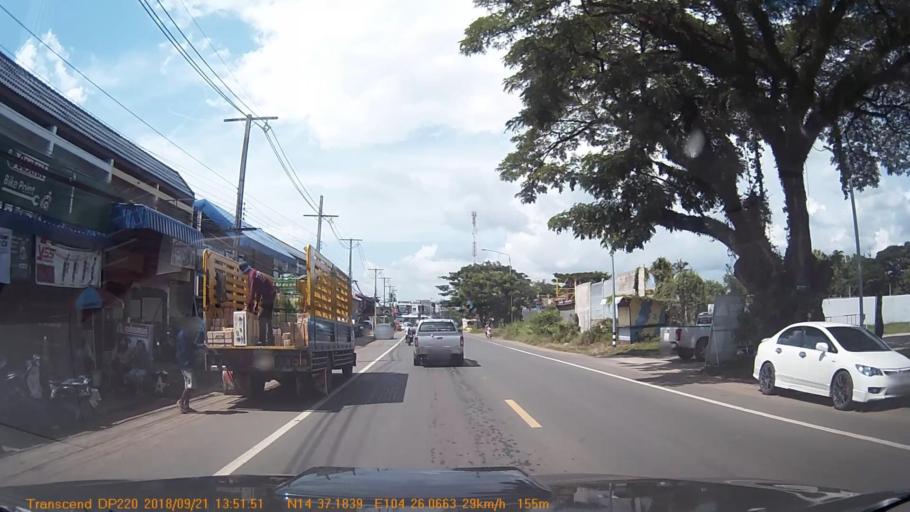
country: TH
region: Sisaket
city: Khun Han
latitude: 14.6199
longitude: 104.4344
